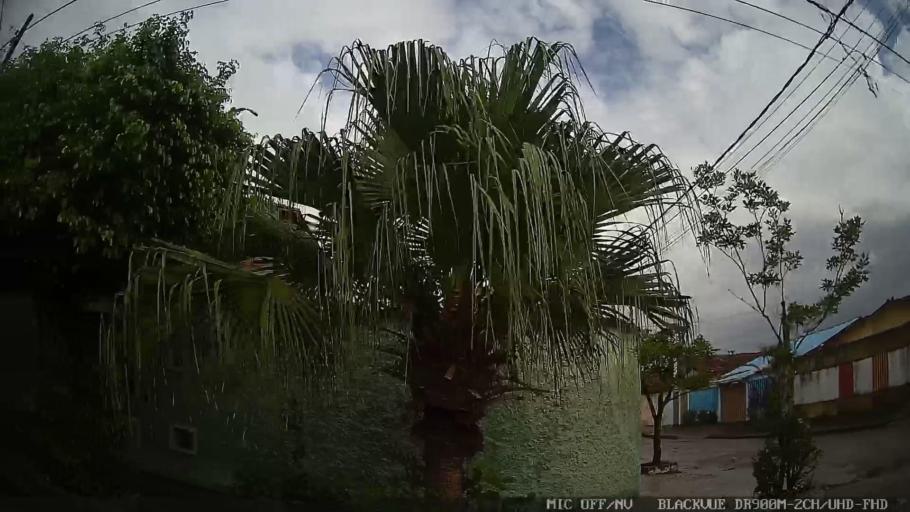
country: BR
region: Sao Paulo
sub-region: Itanhaem
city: Itanhaem
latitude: -24.1884
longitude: -46.8099
